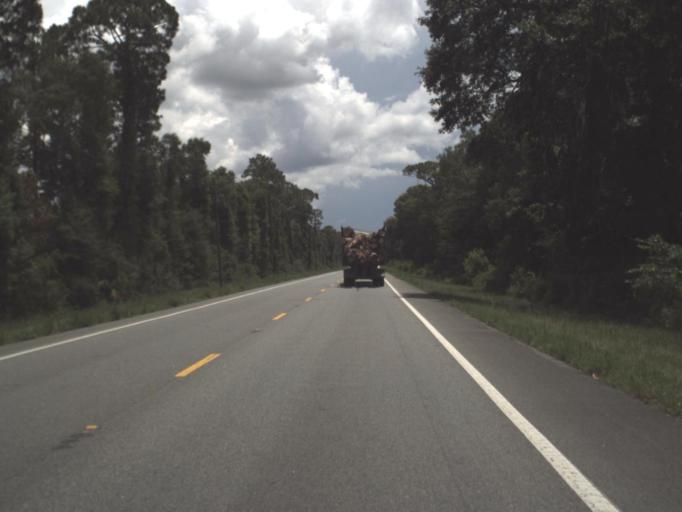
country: US
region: Florida
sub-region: Taylor County
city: Perry
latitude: 30.1015
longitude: -83.6982
